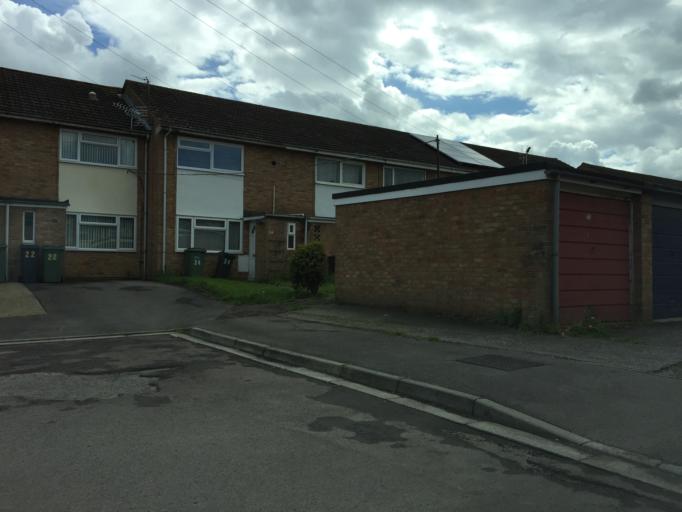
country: GB
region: England
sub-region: Gloucestershire
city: Stonehouse
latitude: 51.7552
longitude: -2.2862
